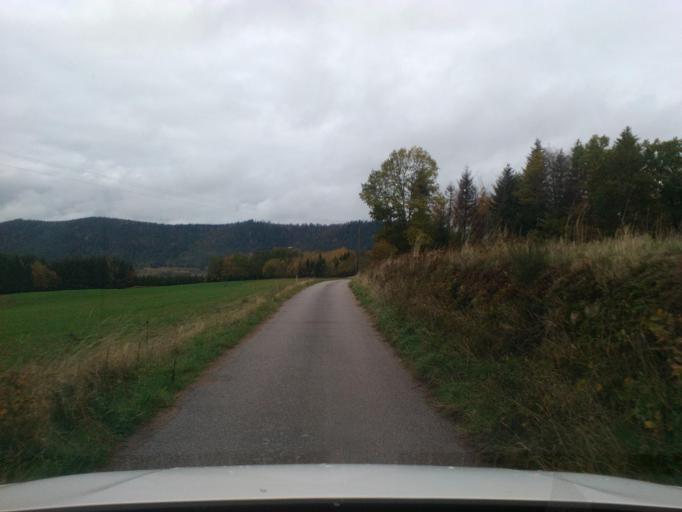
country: FR
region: Lorraine
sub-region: Departement des Vosges
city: Senones
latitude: 48.3824
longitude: 6.9879
